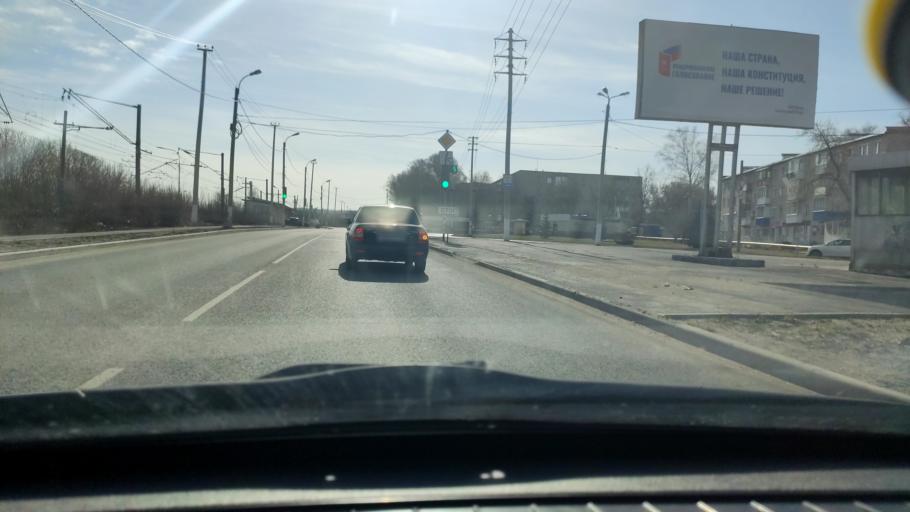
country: RU
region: Samara
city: Zhigulevsk
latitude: 53.4064
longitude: 49.4901
